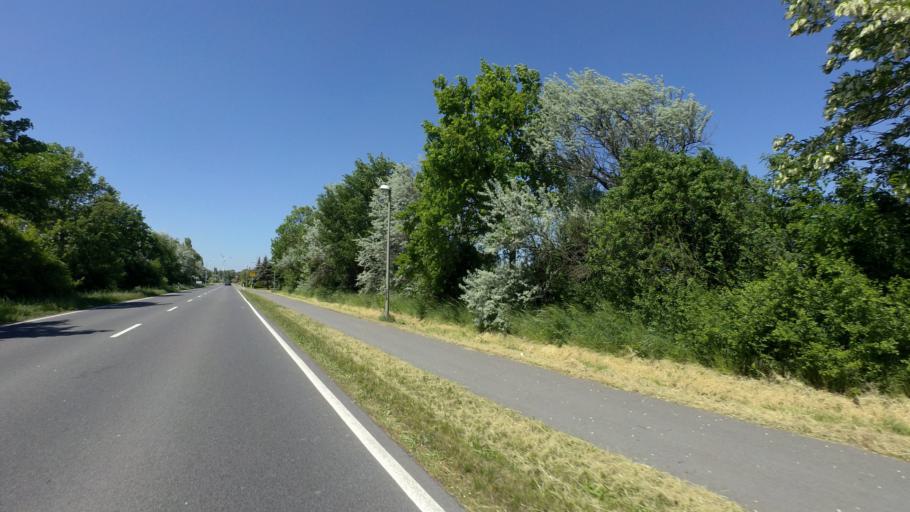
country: DE
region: Brandenburg
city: Drehnow
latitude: 51.8666
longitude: 14.3883
